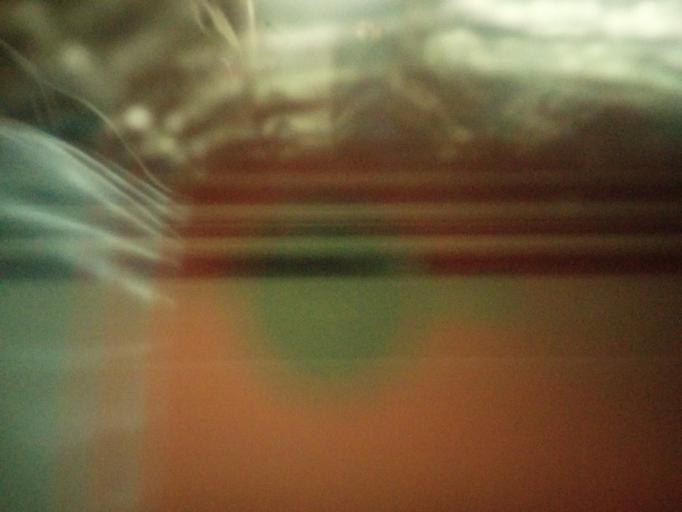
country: JP
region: Kanagawa
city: Odawara
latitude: 35.2034
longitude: 139.1350
